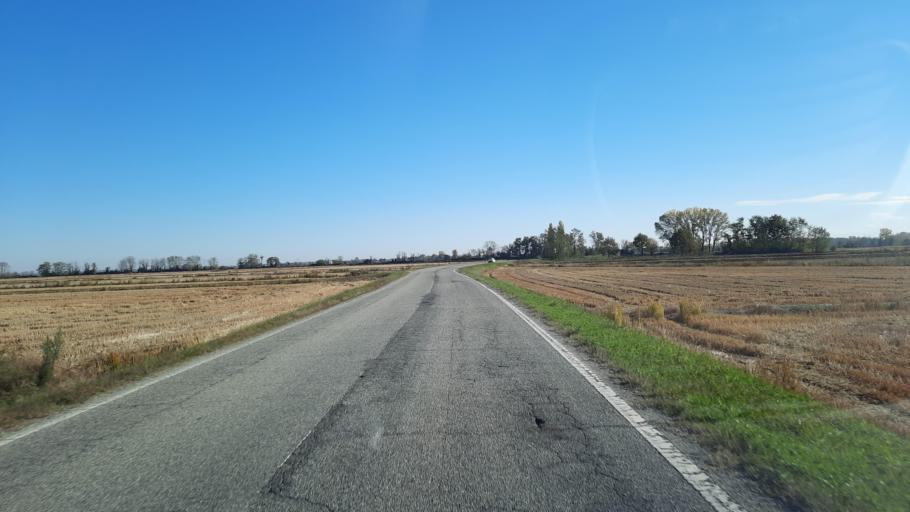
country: IT
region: Piedmont
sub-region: Provincia di Alessandria
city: Villanova Monferrato
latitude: 45.1836
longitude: 8.4424
